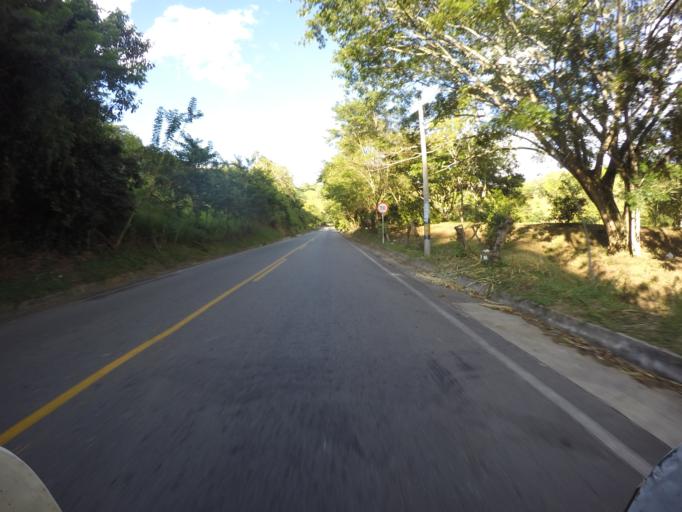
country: CO
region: Valle del Cauca
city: Alcala
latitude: 4.7058
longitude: -75.8412
